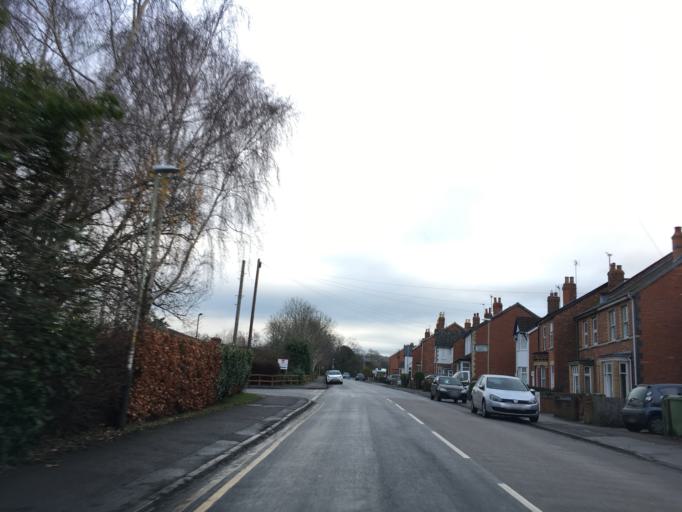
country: GB
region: England
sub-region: Gloucestershire
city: Cheltenham
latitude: 51.8797
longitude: -2.0738
